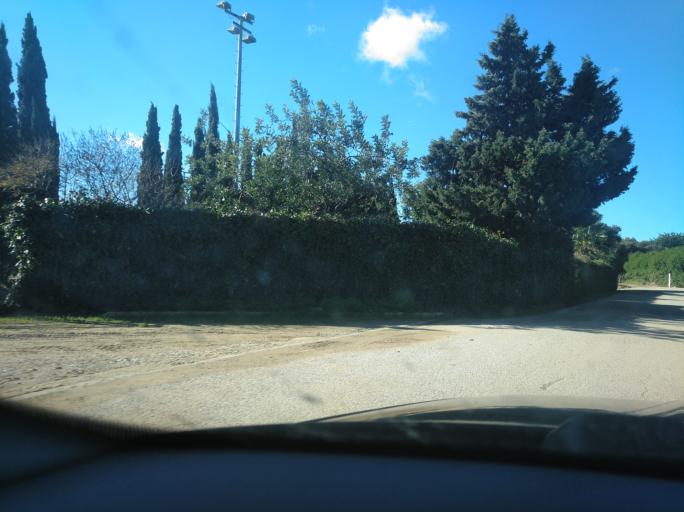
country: PT
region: Faro
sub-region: Tavira
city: Tavira
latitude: 37.1578
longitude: -7.5701
